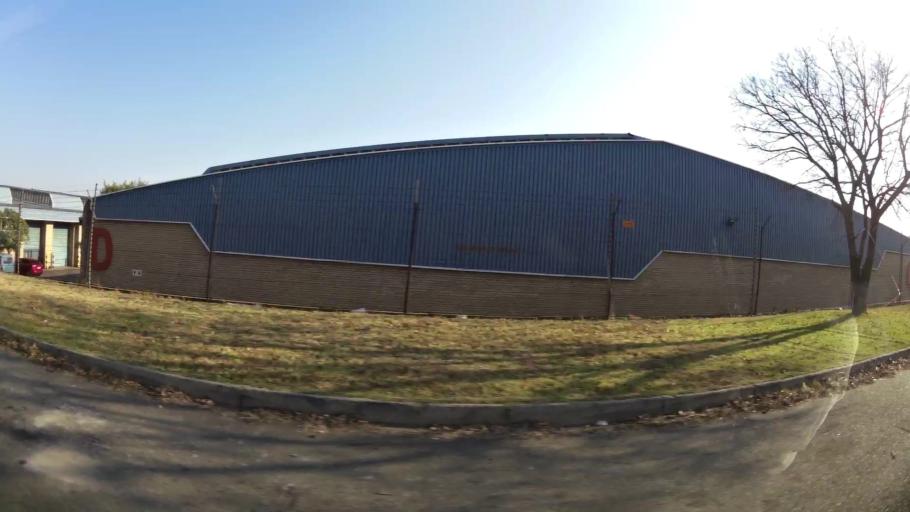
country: ZA
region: Gauteng
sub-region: City of Johannesburg Metropolitan Municipality
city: Modderfontein
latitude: -26.1460
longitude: 28.1859
